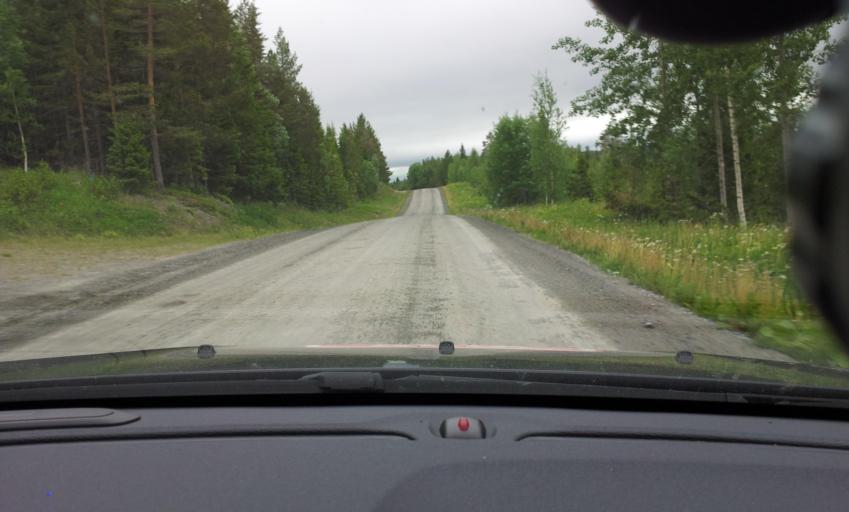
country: SE
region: Jaemtland
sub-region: Are Kommun
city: Jarpen
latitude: 63.2561
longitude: 13.6525
